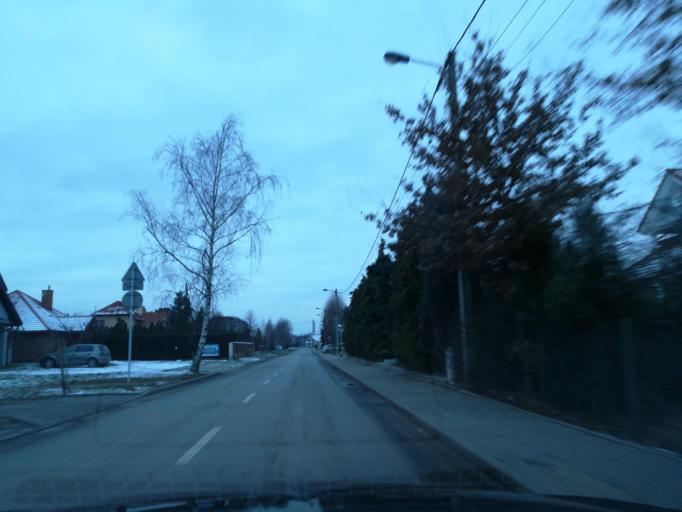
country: PL
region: Subcarpathian Voivodeship
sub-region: Rzeszow
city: Rzeszow
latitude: 50.0144
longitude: 22.0098
